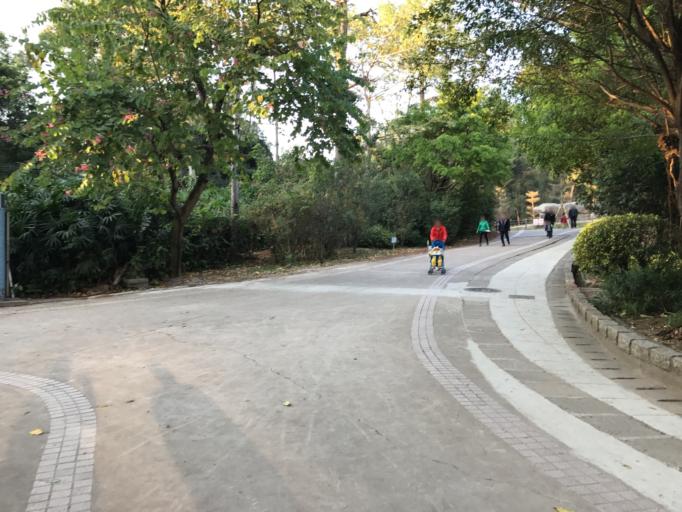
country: CN
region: Guangdong
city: Wushan
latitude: 23.1401
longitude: 113.3016
